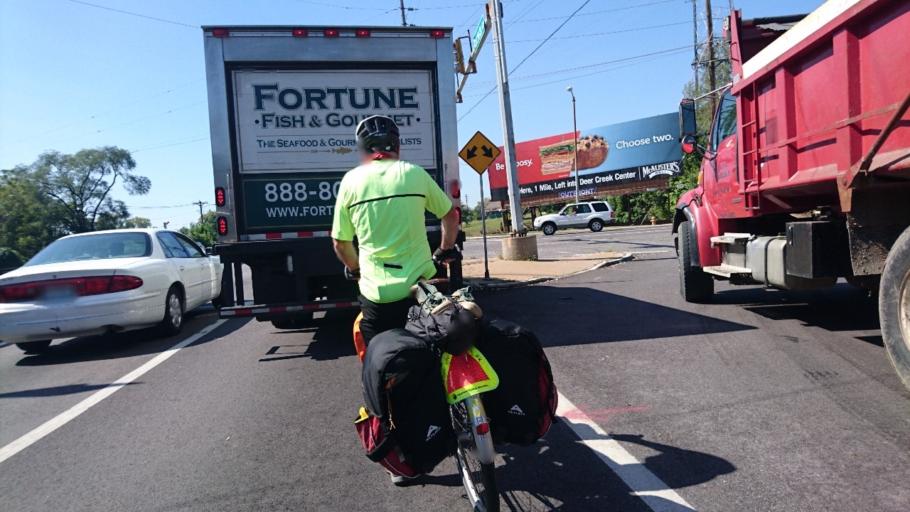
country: US
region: Missouri
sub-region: Saint Louis County
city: Maplewood
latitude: 38.6130
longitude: -90.3333
